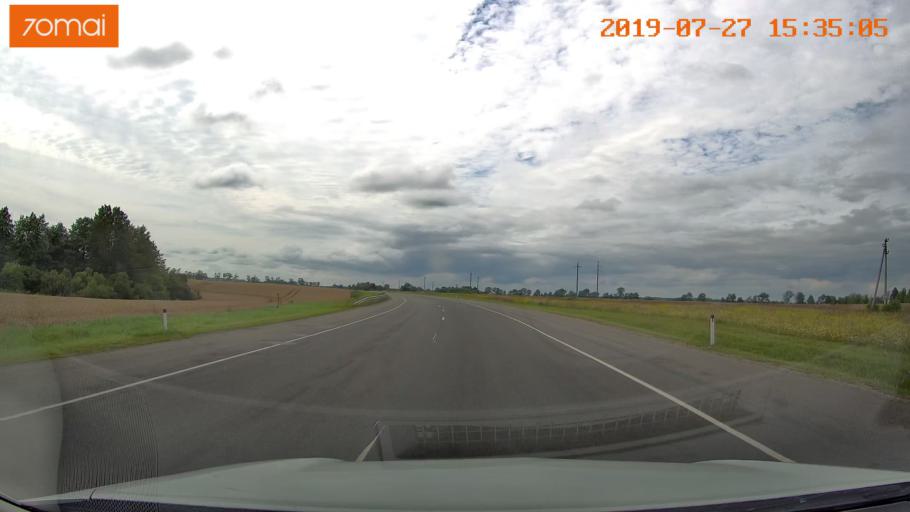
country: RU
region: Kaliningrad
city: Nesterov
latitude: 54.6139
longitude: 22.4066
